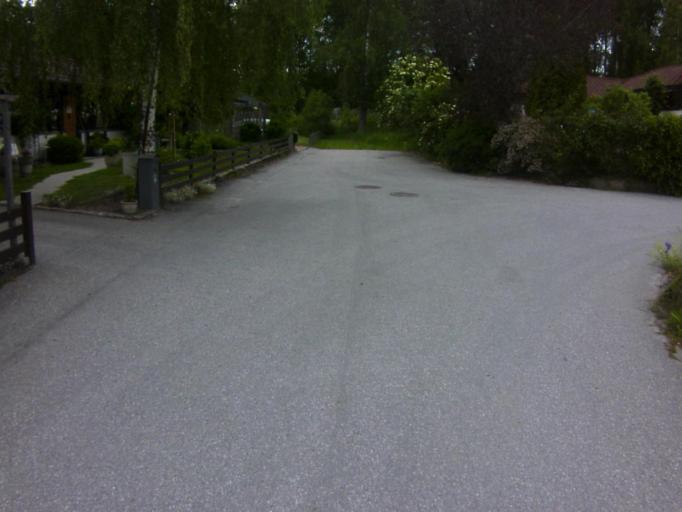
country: SE
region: Soedermanland
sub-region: Eskilstuna Kommun
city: Skogstorp
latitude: 59.3204
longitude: 16.4727
